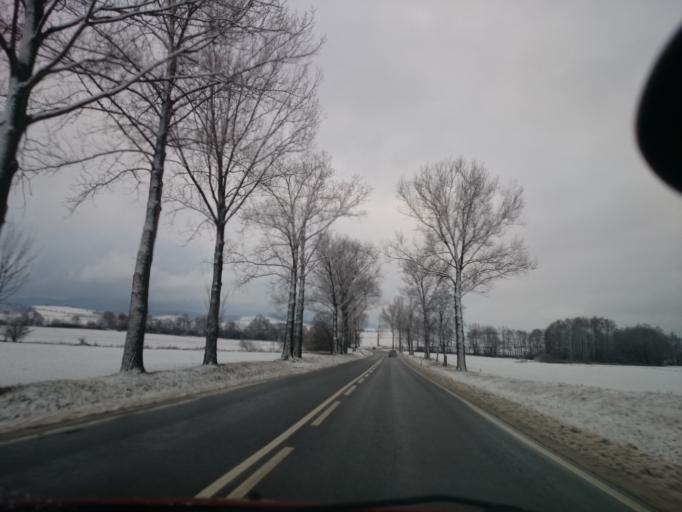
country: PL
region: Lower Silesian Voivodeship
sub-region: Powiat klodzki
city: Bystrzyca Klodzka
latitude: 50.3377
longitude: 16.6623
